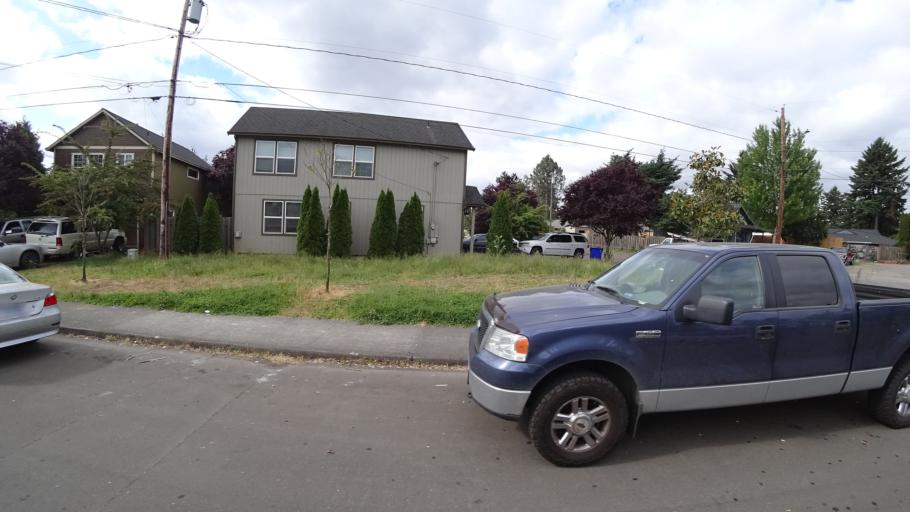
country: US
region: Oregon
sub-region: Multnomah County
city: Lents
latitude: 45.4762
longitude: -122.5618
